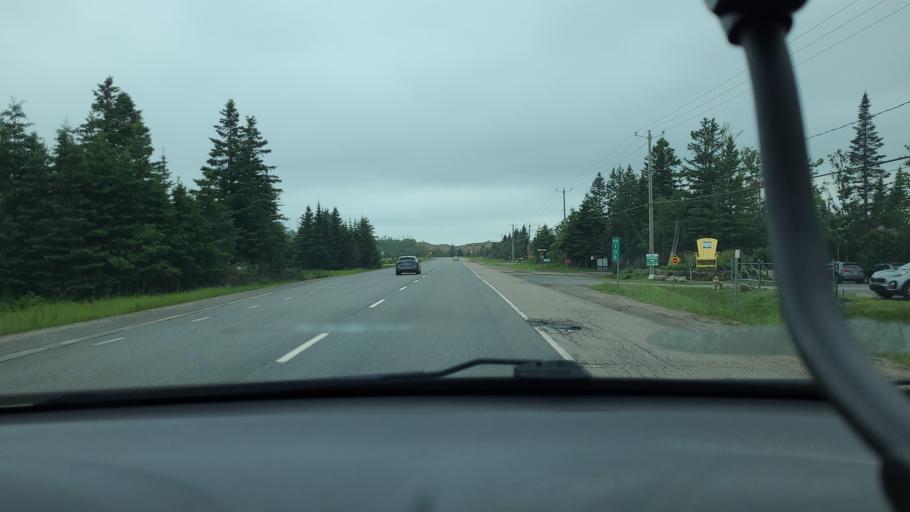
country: CA
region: Quebec
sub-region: Laurentides
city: Mont-Tremblant
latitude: 46.1225
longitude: -74.4551
